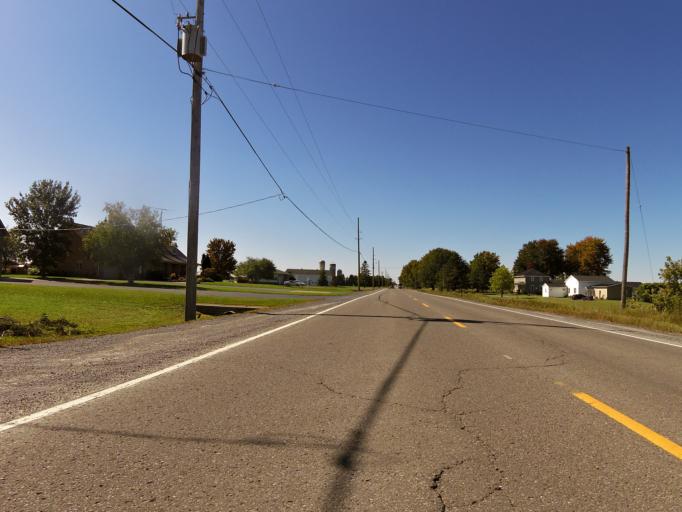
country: CA
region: Ontario
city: Casselman
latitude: 45.2458
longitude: -75.1525
